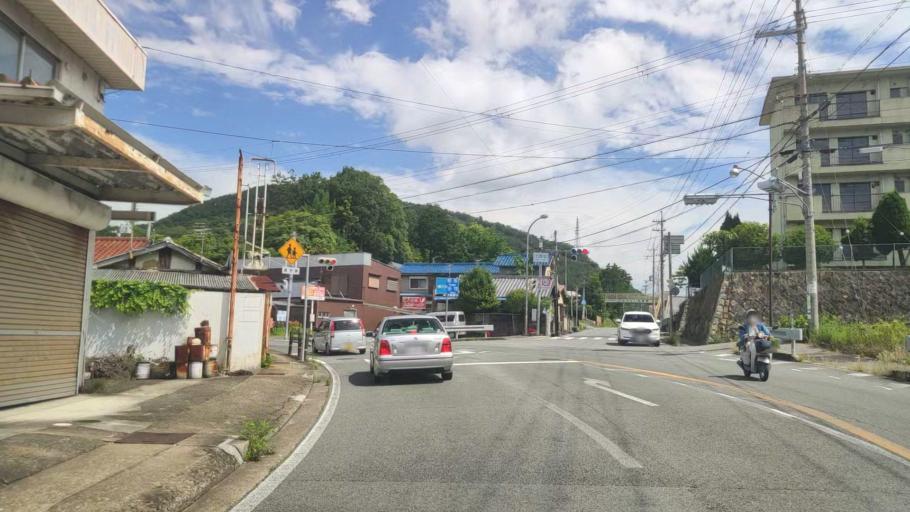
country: JP
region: Hyogo
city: Nishiwaki
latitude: 34.9895
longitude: 134.9787
